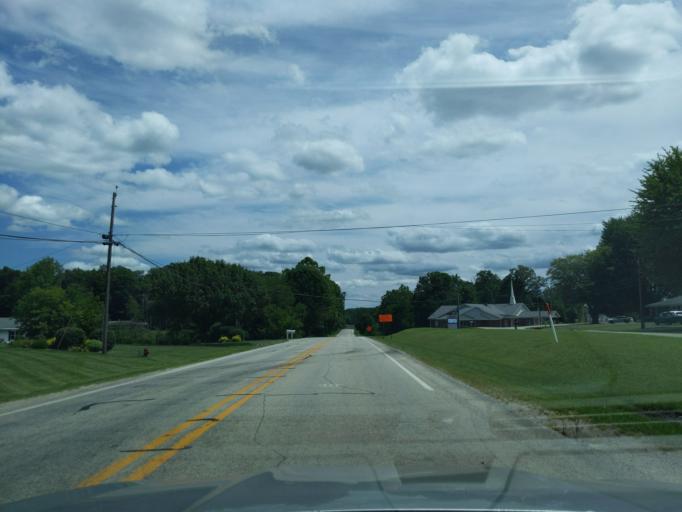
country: US
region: Indiana
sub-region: Ripley County
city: Batesville
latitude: 39.3085
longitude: -85.2477
